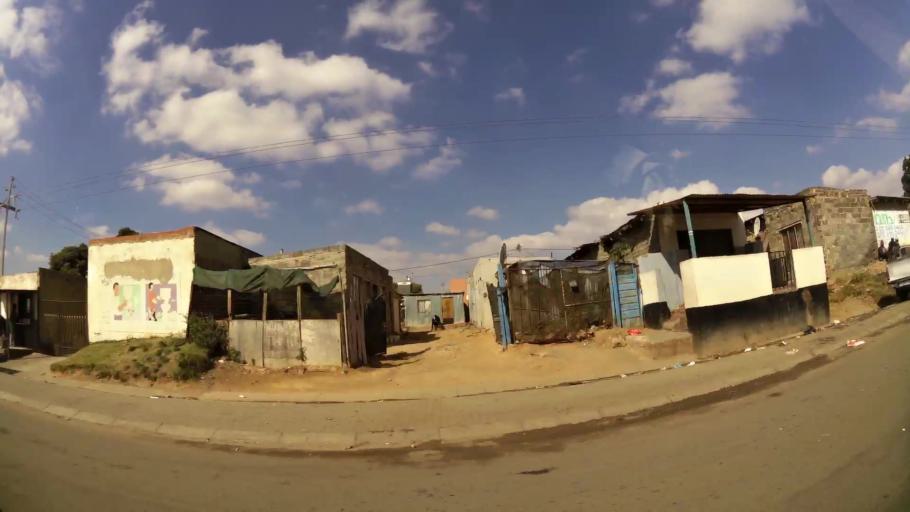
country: ZA
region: Gauteng
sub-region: Ekurhuleni Metropolitan Municipality
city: Tembisa
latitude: -26.0094
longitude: 28.1806
